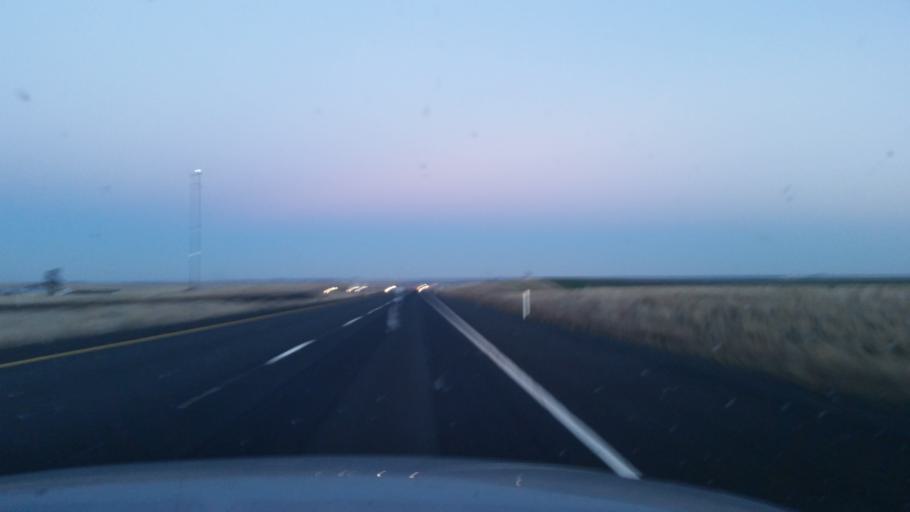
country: US
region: Washington
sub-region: Adams County
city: Ritzville
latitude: 47.1111
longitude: -118.4609
